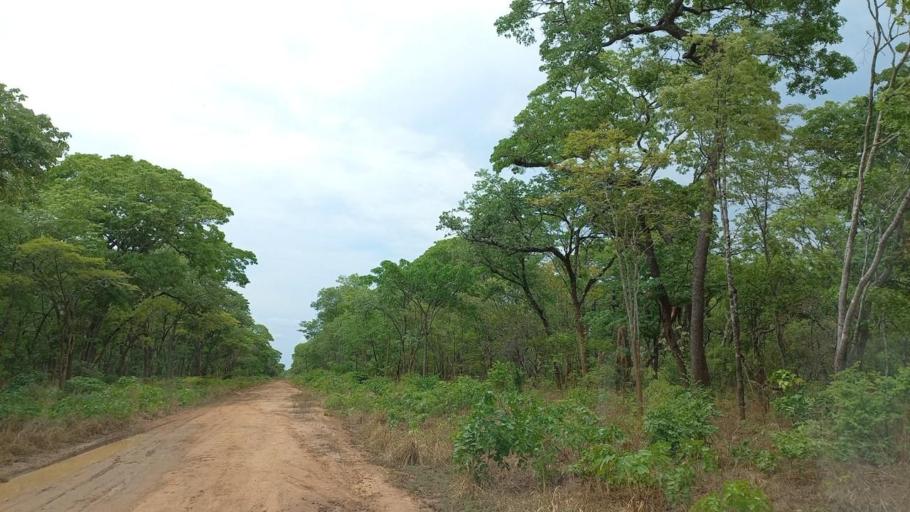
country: ZM
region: North-Western
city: Kalengwa
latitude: -13.5717
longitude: 24.9705
